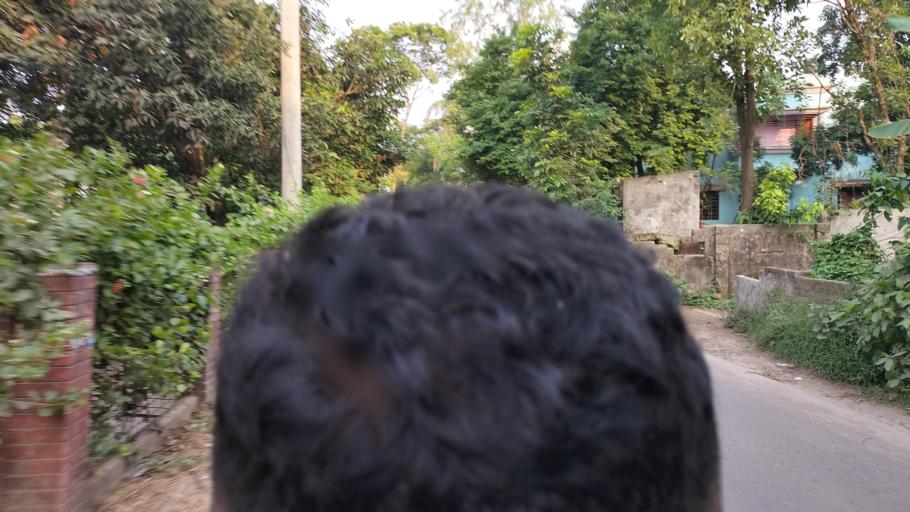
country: BD
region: Dhaka
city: Azimpur
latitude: 23.6654
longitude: 90.3293
